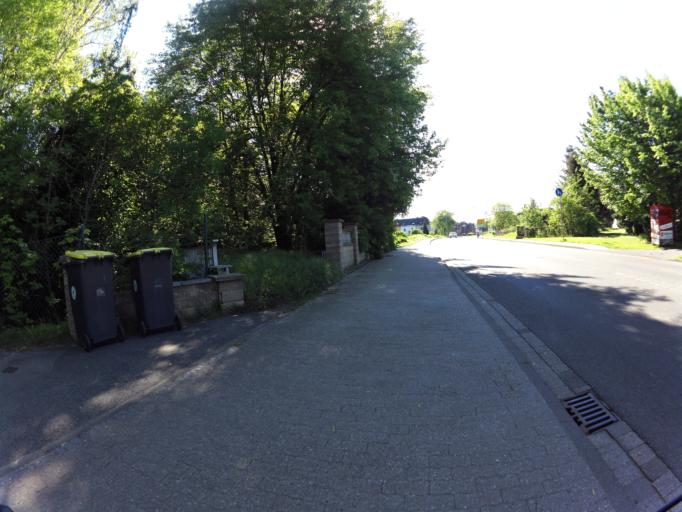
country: DE
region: North Rhine-Westphalia
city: Julich
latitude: 50.9300
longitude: 6.3187
